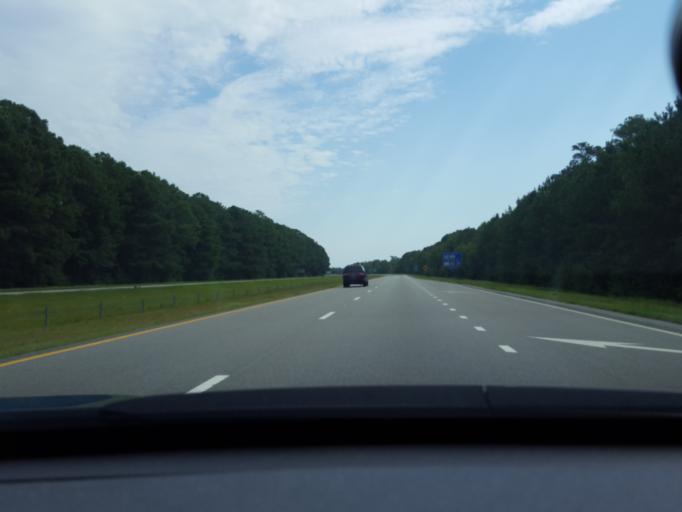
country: US
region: North Carolina
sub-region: Chowan County
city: Edenton
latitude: 36.0702
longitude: -76.6271
